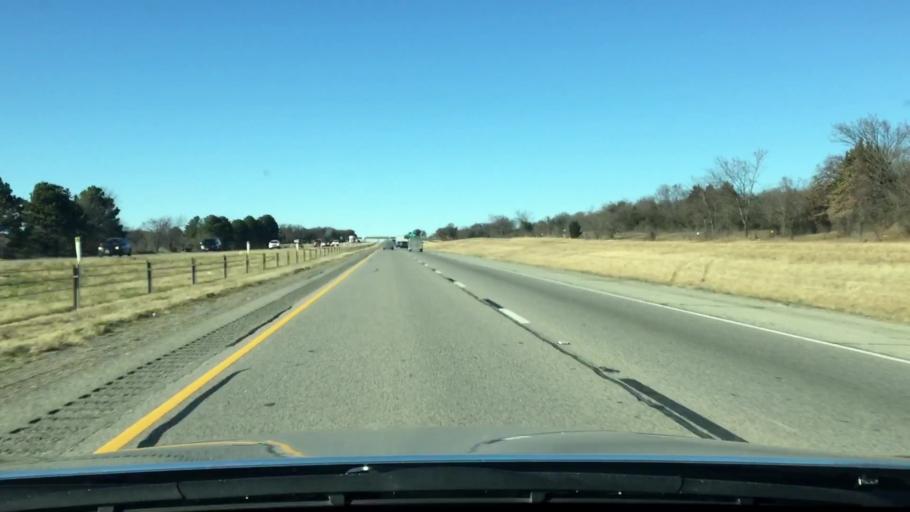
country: US
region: Texas
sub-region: Johnson County
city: Alvarado
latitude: 32.3726
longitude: -97.2029
